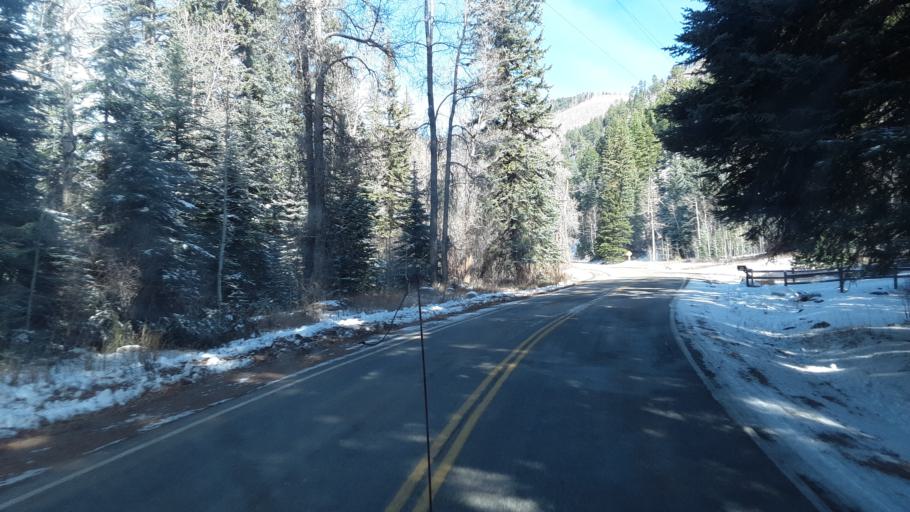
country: US
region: Colorado
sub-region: La Plata County
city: Bayfield
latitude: 37.3708
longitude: -107.6653
